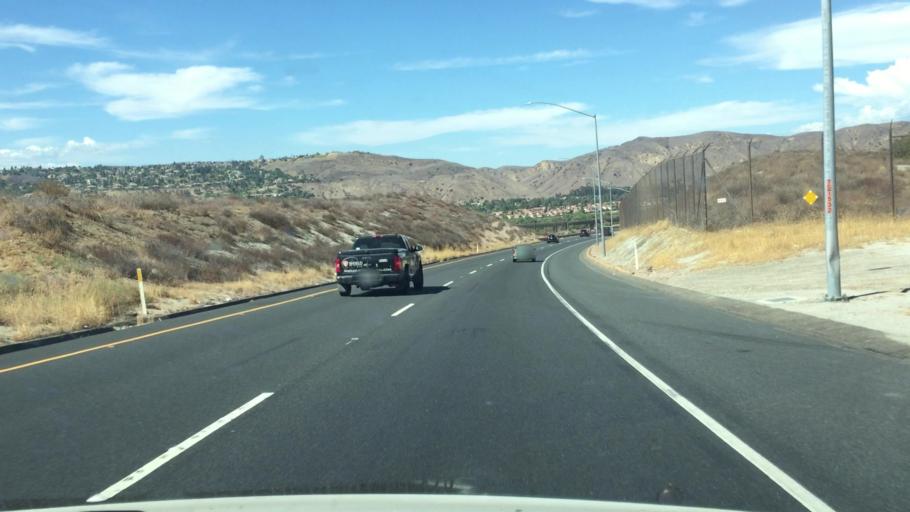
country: US
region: California
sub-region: Orange County
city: Yorba Linda
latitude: 33.8631
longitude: -117.7150
